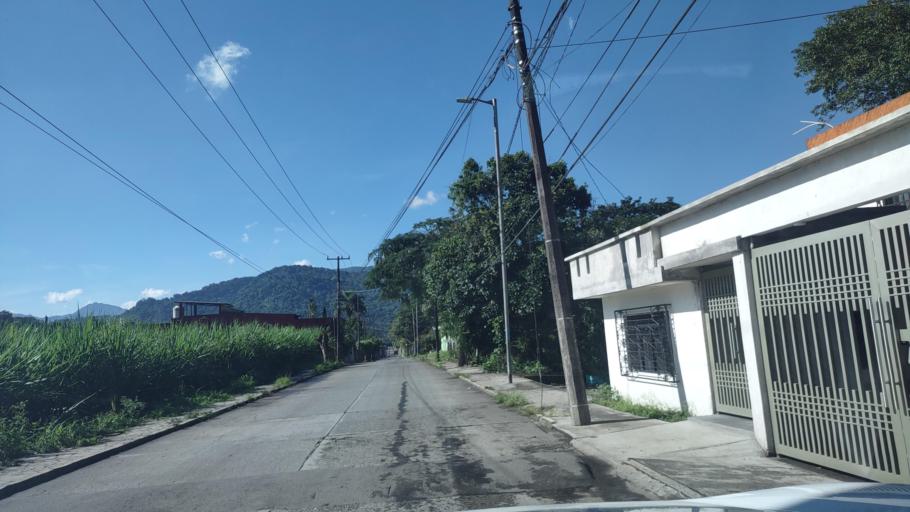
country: MX
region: Veracruz
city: Cuautlapan
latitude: 18.8718
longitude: -97.0225
